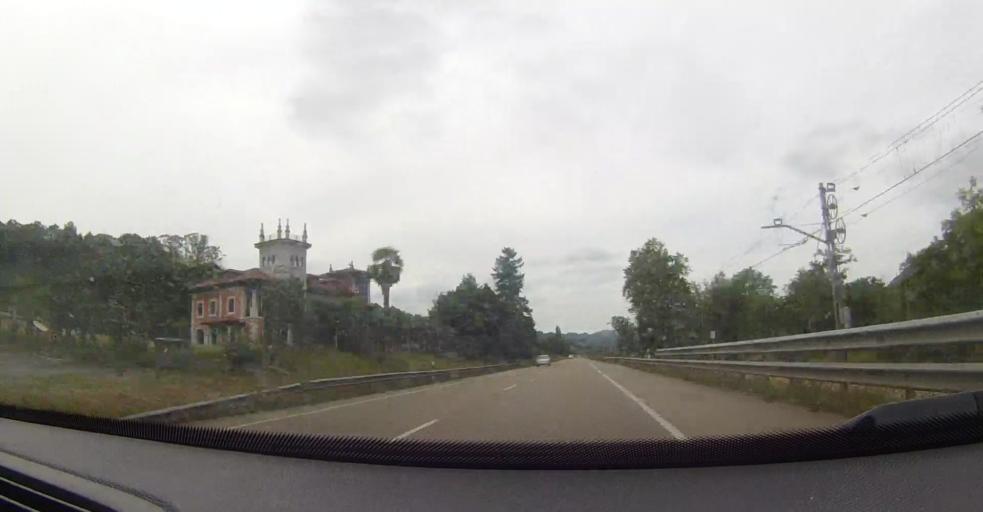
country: ES
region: Asturias
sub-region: Province of Asturias
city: Pilona
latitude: 43.3664
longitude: -5.2787
